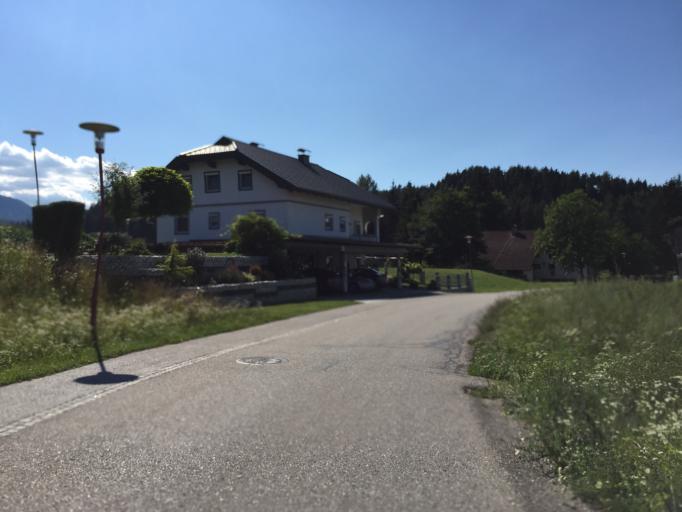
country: AT
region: Carinthia
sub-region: Politischer Bezirk Volkermarkt
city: Feistritz ob Bleiburg
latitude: 46.5615
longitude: 14.7598
